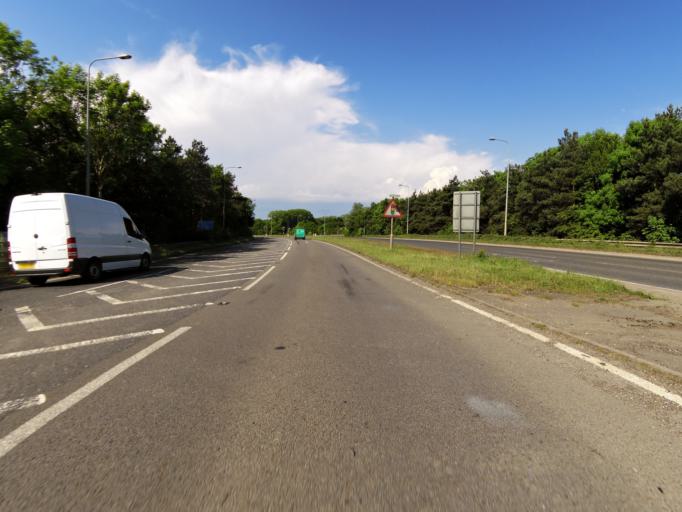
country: GB
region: England
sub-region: Suffolk
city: Bramford
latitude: 52.1032
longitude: 1.1001
